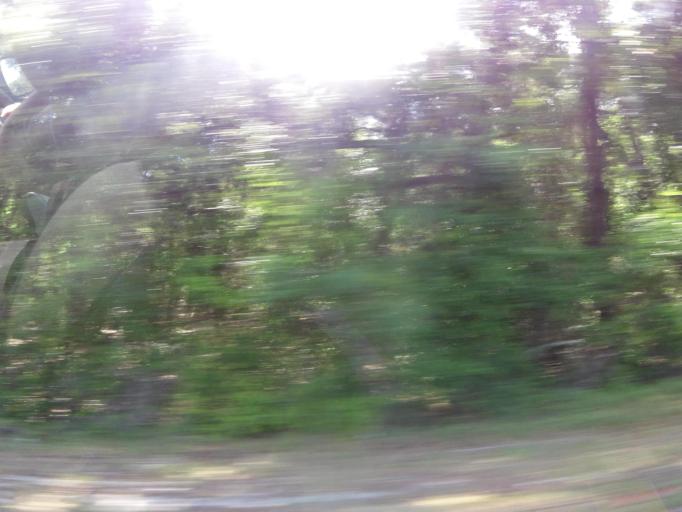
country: US
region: Florida
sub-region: Clay County
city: Keystone Heights
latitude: 29.8306
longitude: -81.9225
